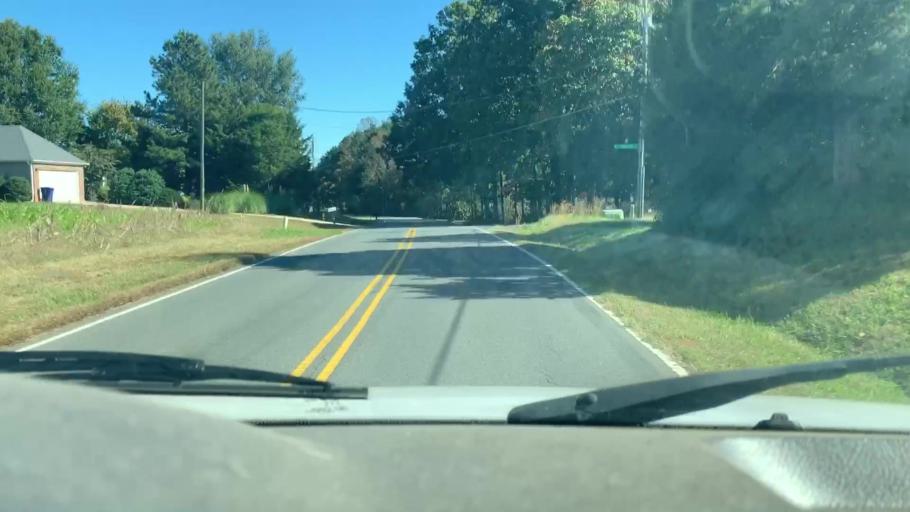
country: US
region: North Carolina
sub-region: Mecklenburg County
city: Cornelius
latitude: 35.4549
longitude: -80.8260
